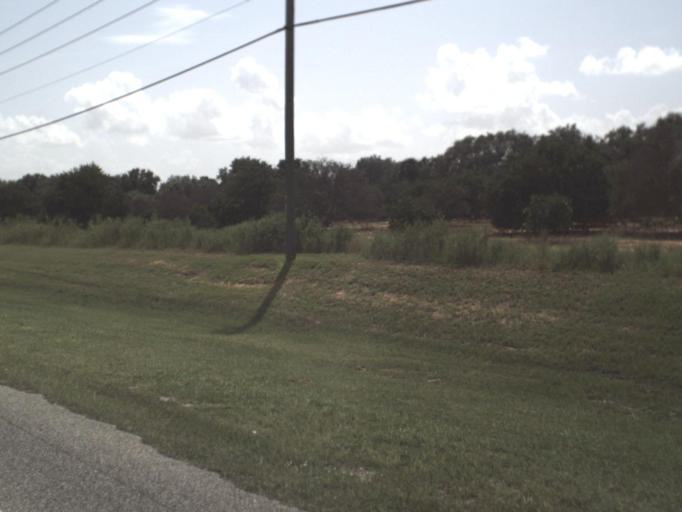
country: US
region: Florida
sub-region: Polk County
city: Davenport
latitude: 28.1719
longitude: -81.6400
